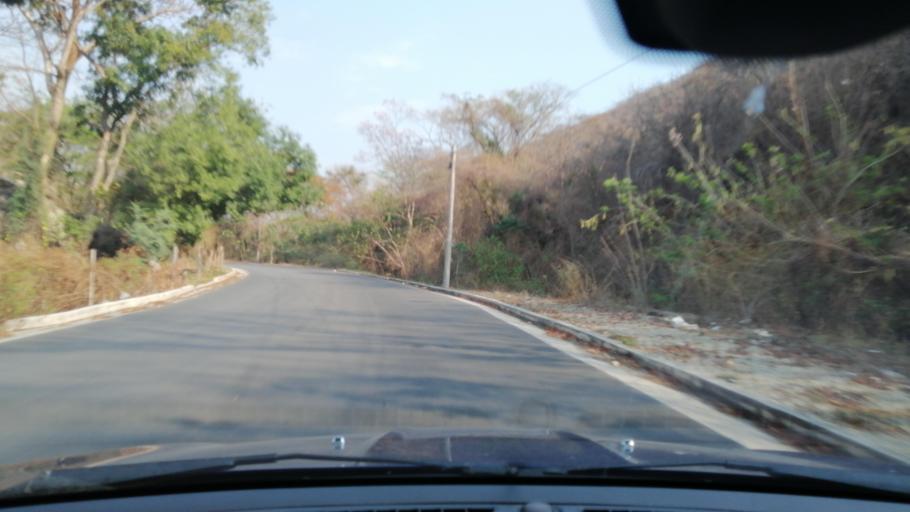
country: SV
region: Santa Ana
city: Metapan
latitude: 14.2307
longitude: -89.4583
